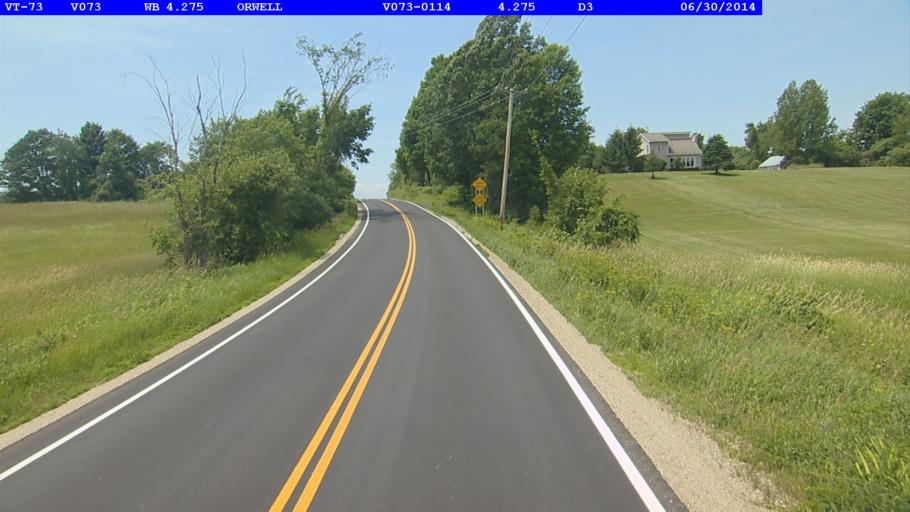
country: US
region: Vermont
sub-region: Rutland County
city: Brandon
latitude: 43.7955
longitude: -73.2252
